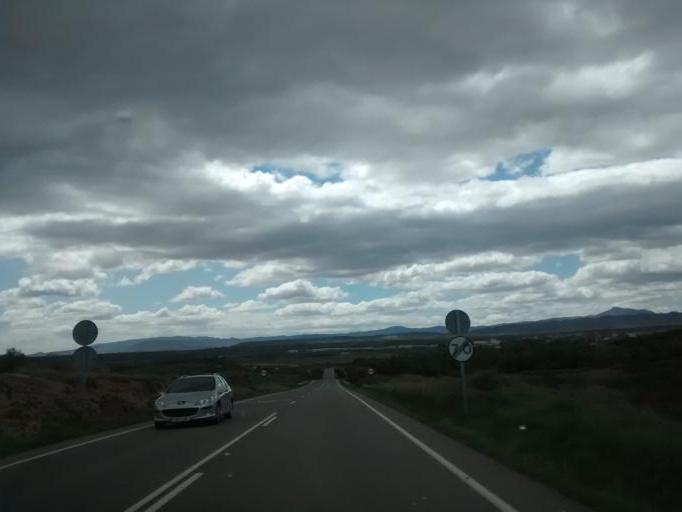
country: ES
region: La Rioja
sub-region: Provincia de La Rioja
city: Pradejon
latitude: 42.3432
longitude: -2.0905
